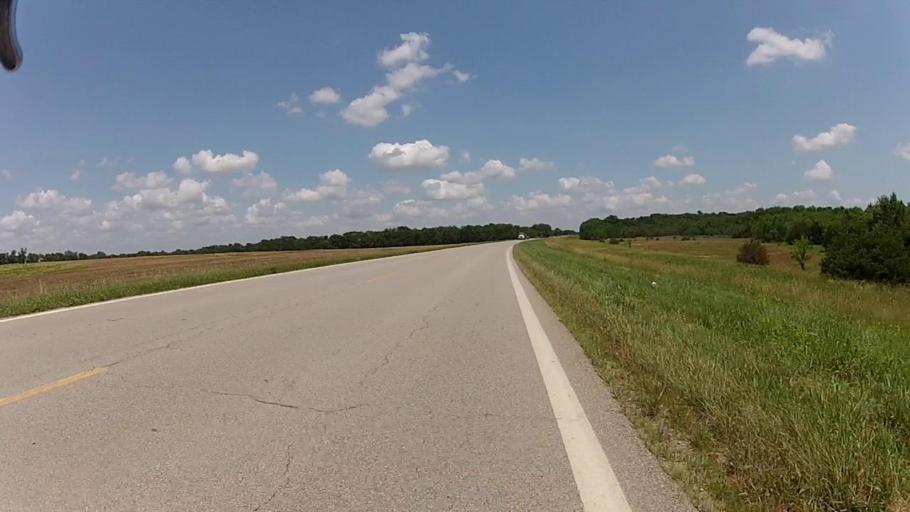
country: US
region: Kansas
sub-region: Labette County
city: Altamont
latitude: 37.1949
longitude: -95.4013
